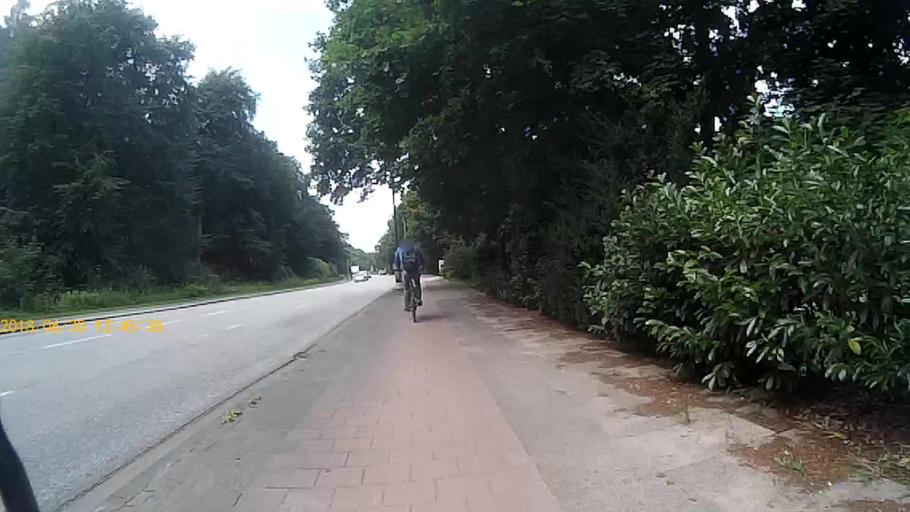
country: DE
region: Hamburg
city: Harburg
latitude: 53.4708
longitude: 9.9088
